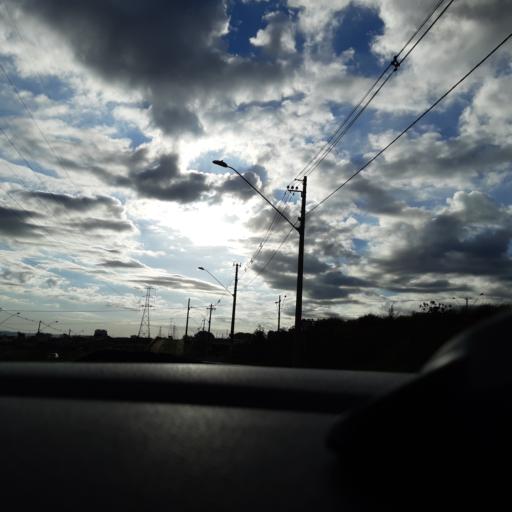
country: BR
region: Sao Paulo
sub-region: Ourinhos
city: Ourinhos
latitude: -23.0007
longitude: -49.8437
